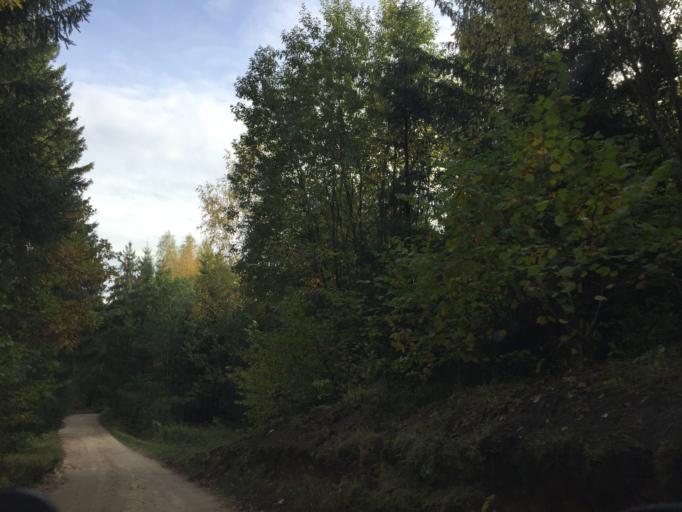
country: LV
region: Jaunpils
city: Jaunpils
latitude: 56.5844
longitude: 23.0132
